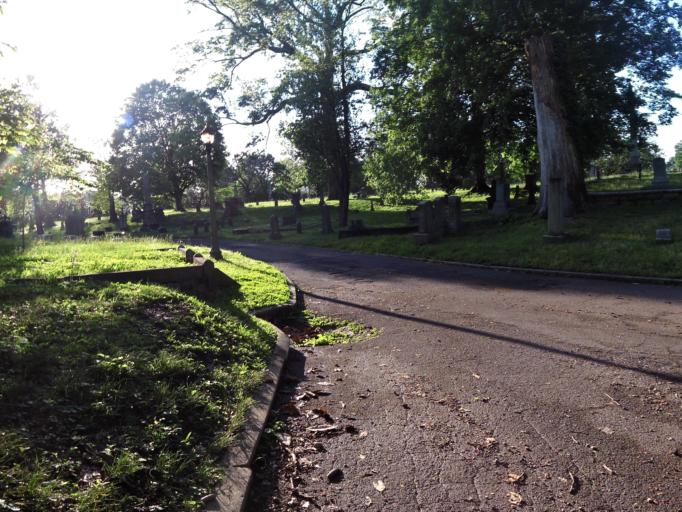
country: US
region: Tennessee
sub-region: Knox County
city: Knoxville
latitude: 35.9733
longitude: -83.9257
